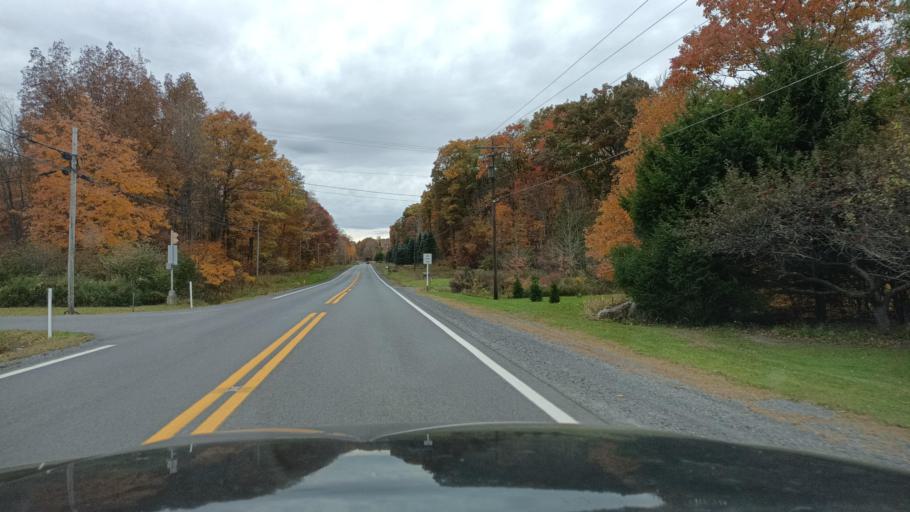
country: US
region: Maryland
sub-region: Garrett County
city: Mountain Lake Park
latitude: 39.2752
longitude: -79.2797
